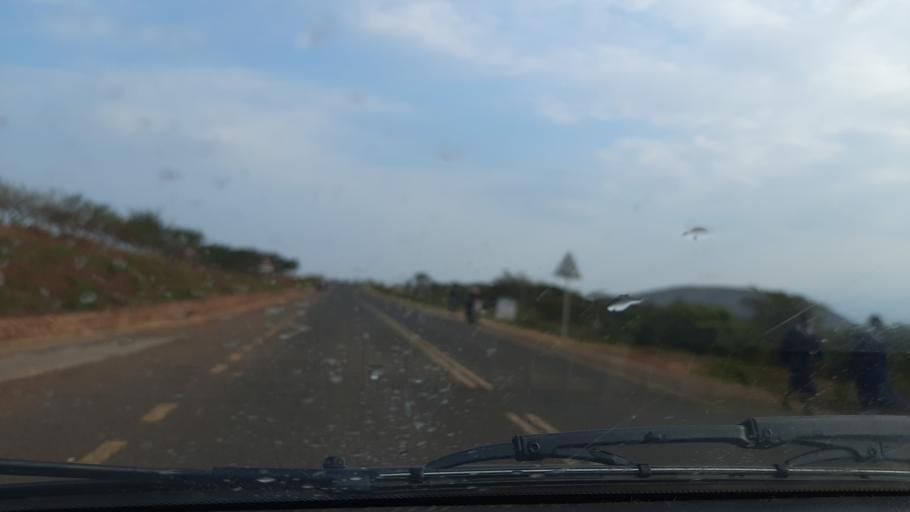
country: TZ
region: Arusha
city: Kingori
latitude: -3.0445
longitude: 37.0500
